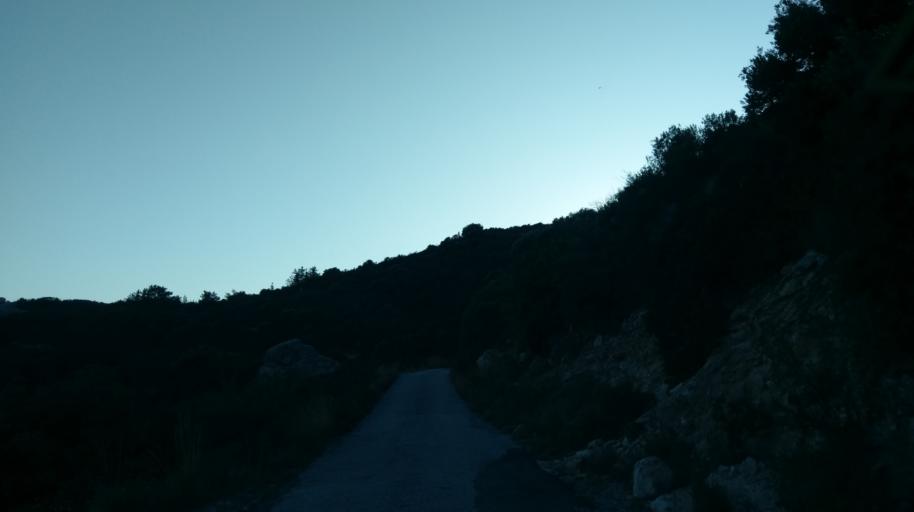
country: CY
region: Ammochostos
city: Trikomo
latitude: 35.3823
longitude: 33.8993
